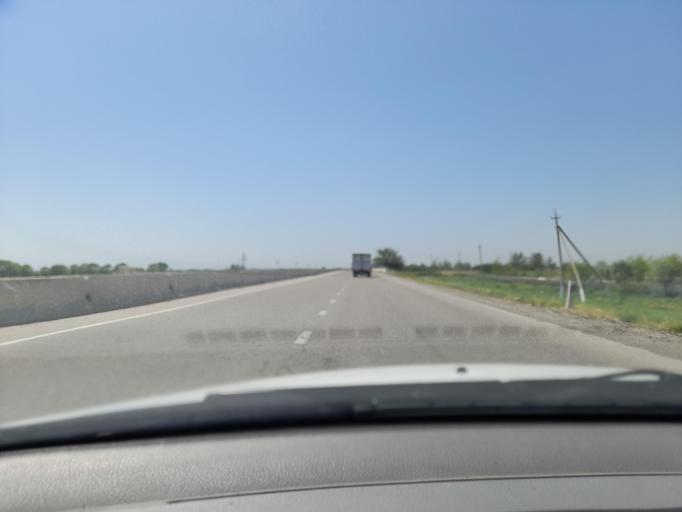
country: UZ
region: Jizzax
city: Dustlik
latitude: 40.4225
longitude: 68.2155
